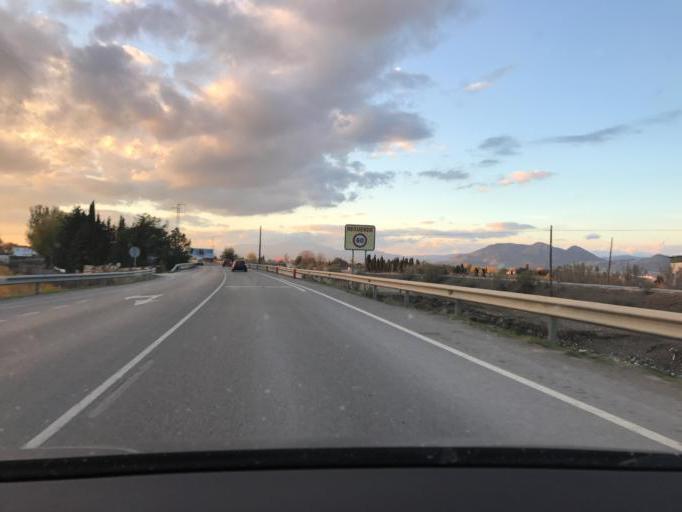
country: ES
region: Andalusia
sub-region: Provincia de Granada
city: Cullar-Vega
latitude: 37.1720
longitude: -3.6511
